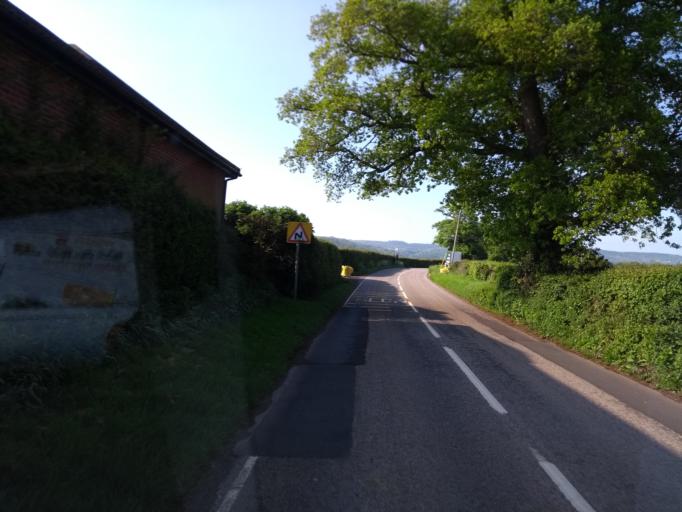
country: GB
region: England
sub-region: Somerset
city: Taunton
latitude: 50.9897
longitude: -3.0850
